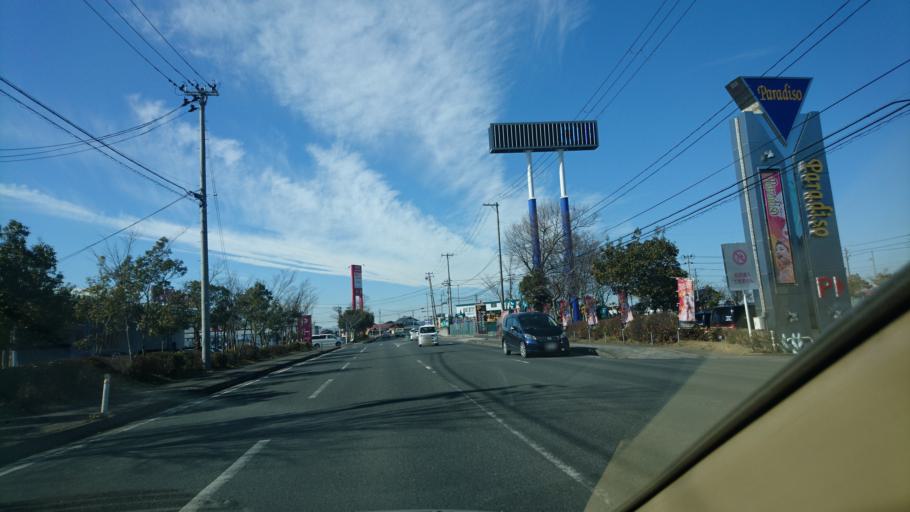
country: JP
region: Miyagi
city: Furukawa
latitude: 38.5994
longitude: 140.9739
